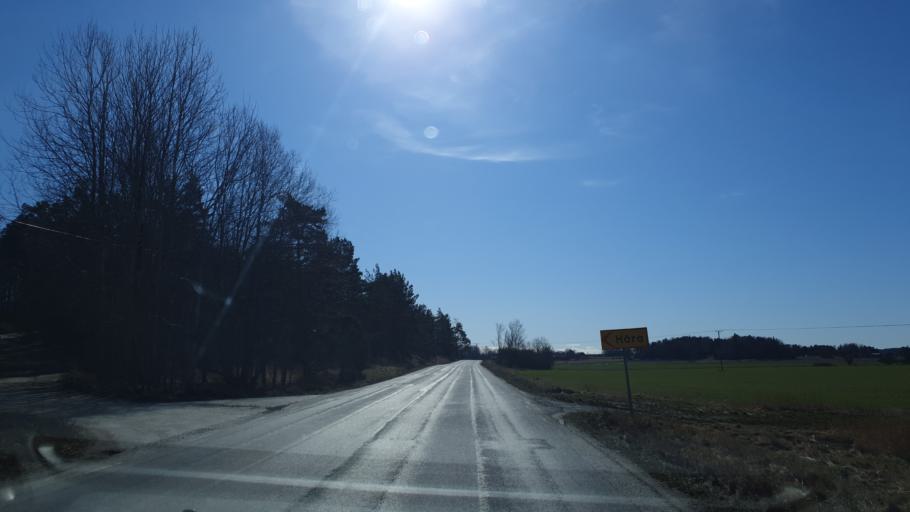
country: SE
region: Uppsala
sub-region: Enkopings Kommun
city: Grillby
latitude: 59.6069
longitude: 17.2756
